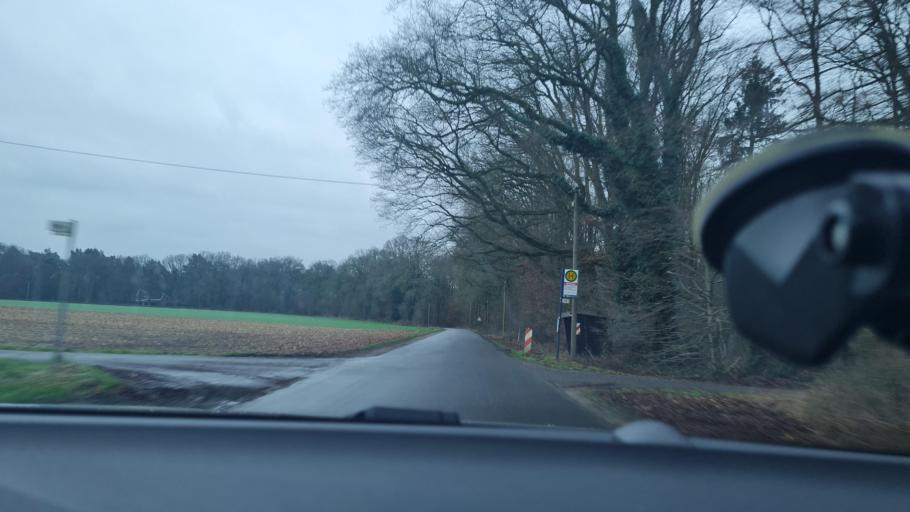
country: DE
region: North Rhine-Westphalia
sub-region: Regierungsbezirk Munster
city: Raesfeld
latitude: 51.7617
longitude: 6.8997
